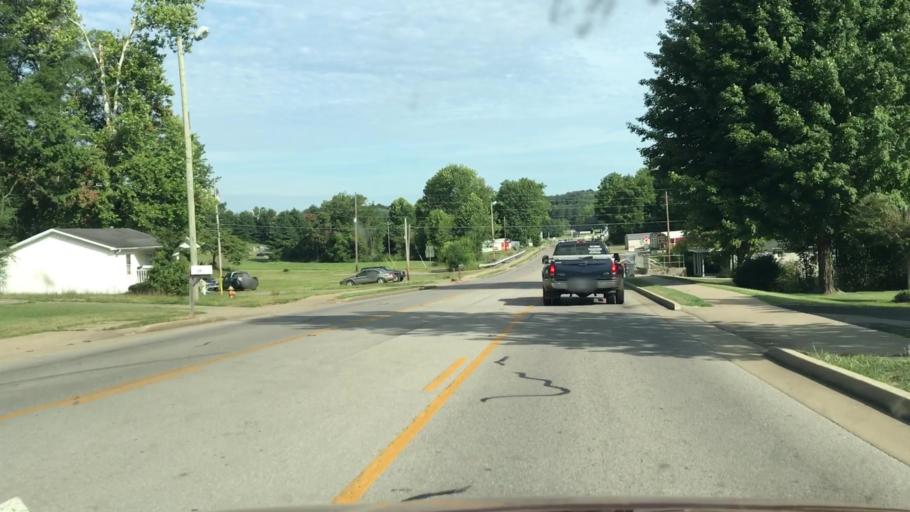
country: US
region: Kentucky
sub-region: Edmonson County
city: Brownsville
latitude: 37.1863
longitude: -86.2510
